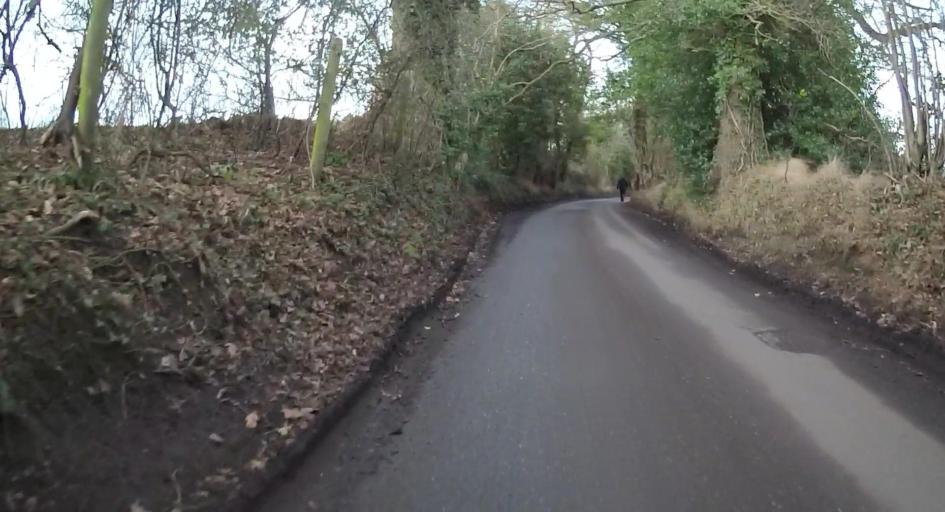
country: GB
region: England
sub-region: Wokingham
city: Wokingham
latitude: 51.3987
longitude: -0.8536
